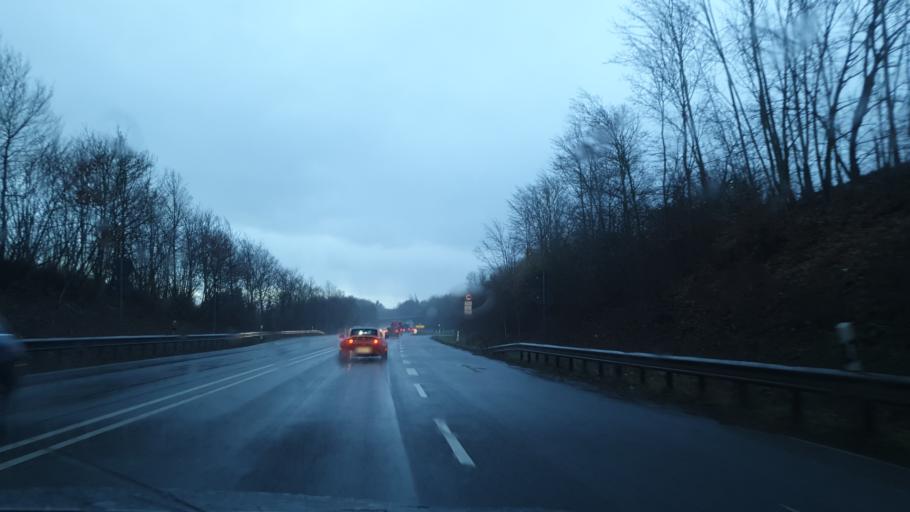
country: DE
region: Rheinland-Pfalz
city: Mendig
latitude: 50.3787
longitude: 7.2702
